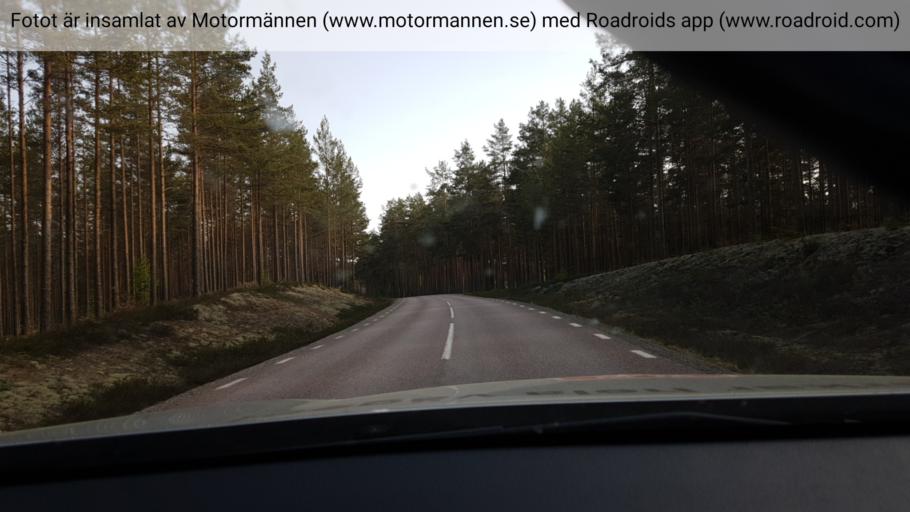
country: SE
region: Gaevleborg
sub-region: Sandvikens Kommun
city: Arsunda
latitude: 60.4647
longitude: 16.7033
